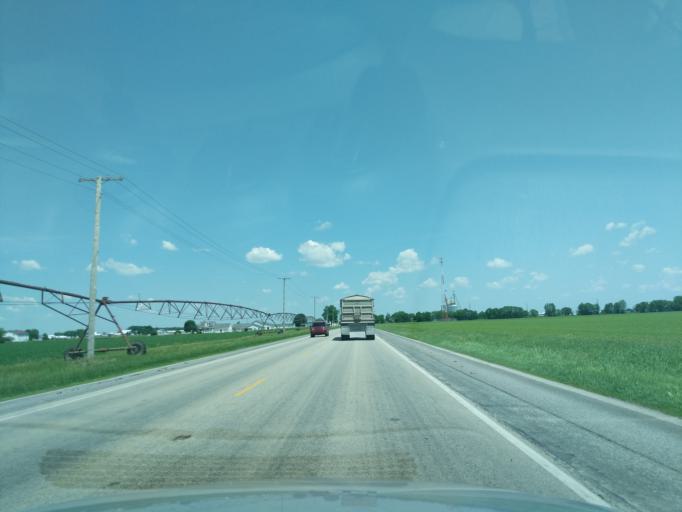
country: US
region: Indiana
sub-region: LaGrange County
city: Topeka
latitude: 41.5290
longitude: -85.5778
